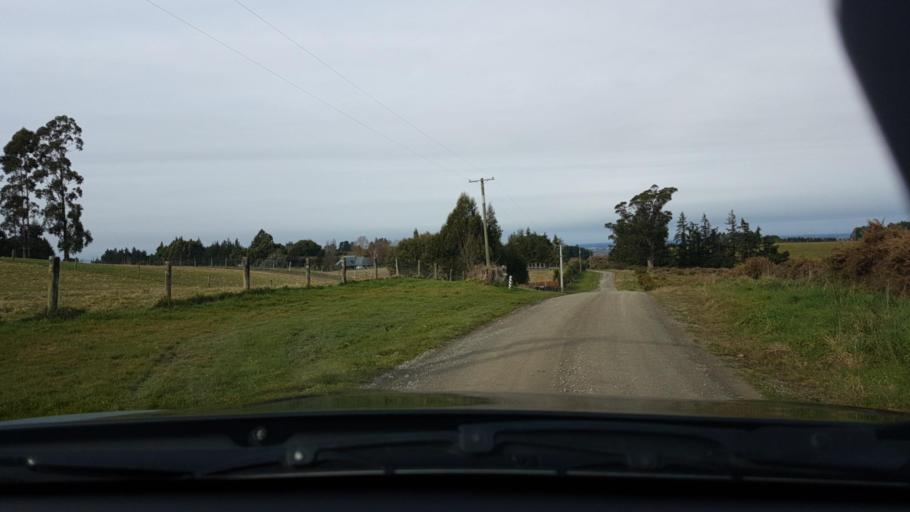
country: NZ
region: Canterbury
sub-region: Waimakariri District
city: Woodend
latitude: -43.2477
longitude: 172.5757
